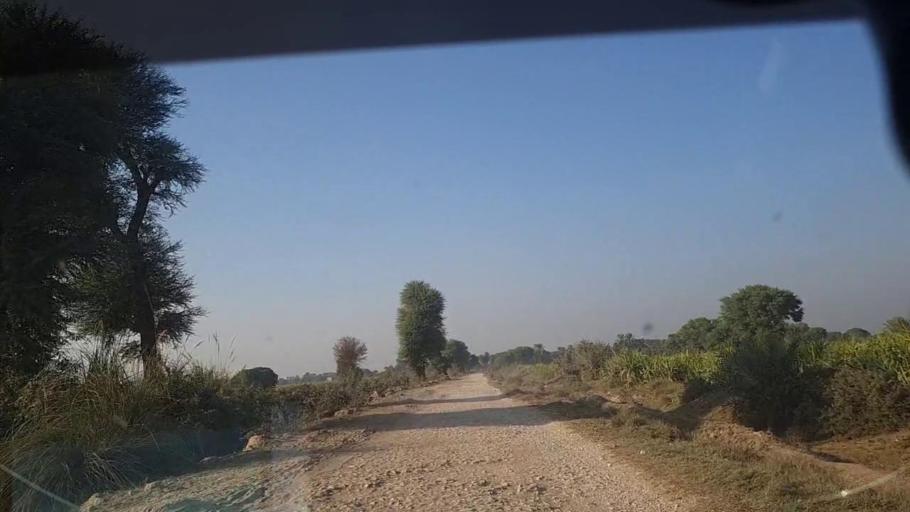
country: PK
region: Sindh
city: Sobhadero
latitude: 27.2639
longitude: 68.3499
